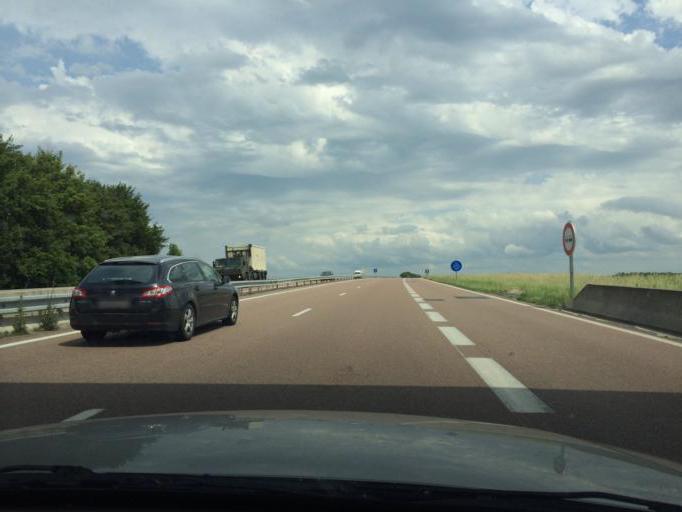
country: FR
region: Champagne-Ardenne
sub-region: Departement de la Marne
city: Jonchery-sur-Vesle
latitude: 49.2318
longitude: 3.8388
